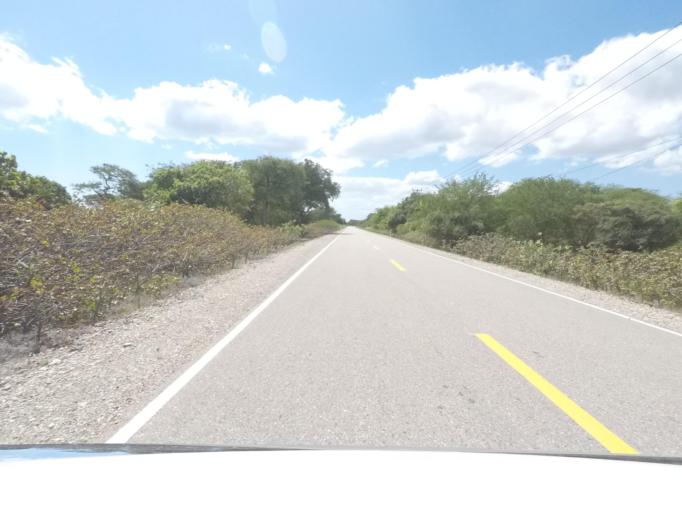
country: TL
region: Baucau
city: Baucau
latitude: -8.4281
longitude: 126.6910
